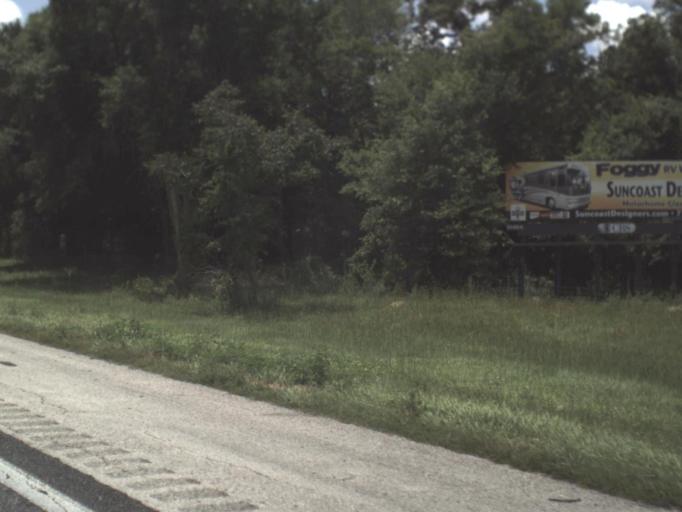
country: US
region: Florida
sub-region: Alachua County
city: High Springs
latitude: 29.8508
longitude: -82.5350
